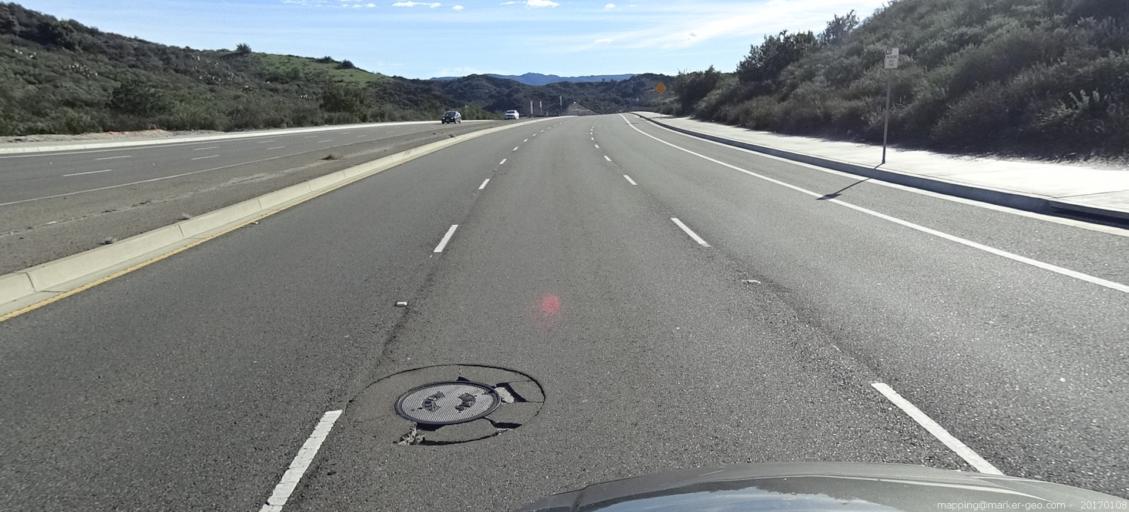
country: US
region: California
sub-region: Orange County
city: Las Flores
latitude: 33.5870
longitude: -117.6185
